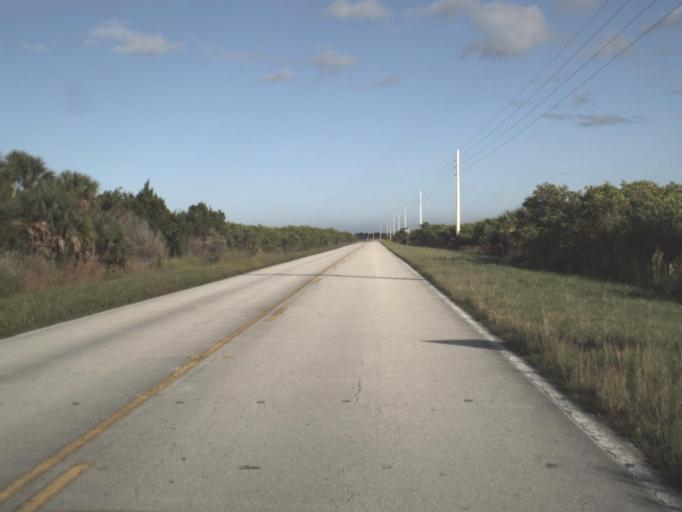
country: US
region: Florida
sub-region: Brevard County
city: Titusville
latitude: 28.6432
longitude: -80.7691
